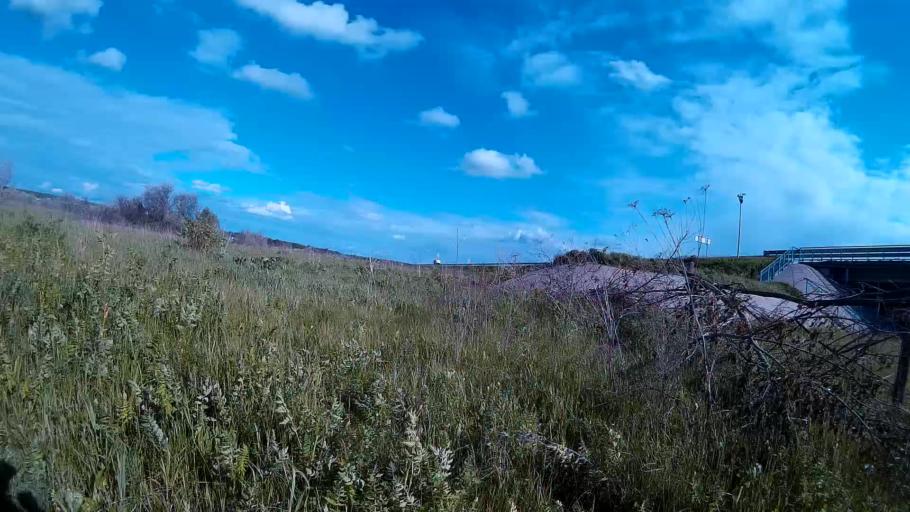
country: RU
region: Ulyanovsk
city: Novoul'yanovsk
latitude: 54.2240
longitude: 48.2639
